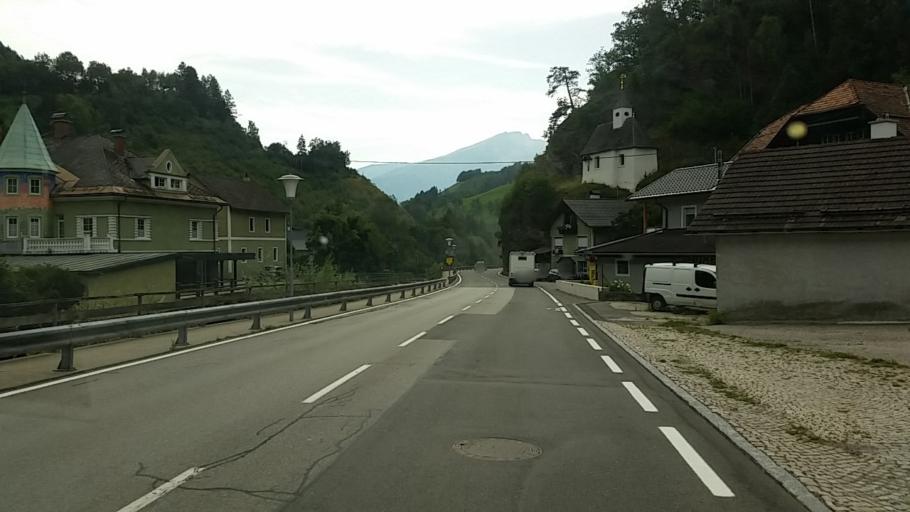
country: AT
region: Carinthia
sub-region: Politischer Bezirk Spittal an der Drau
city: Gmuend
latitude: 46.9223
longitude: 13.5763
